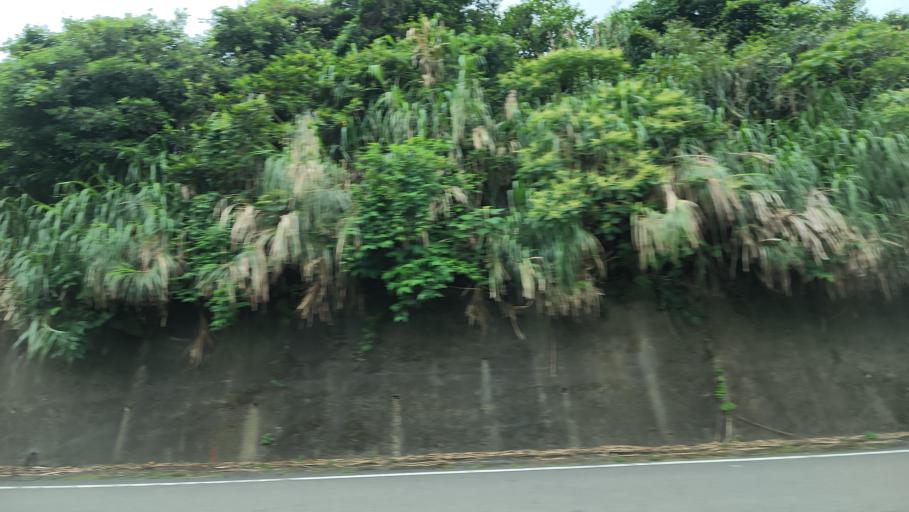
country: TW
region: Taiwan
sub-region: Keelung
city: Keelung
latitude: 25.1982
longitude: 121.6827
